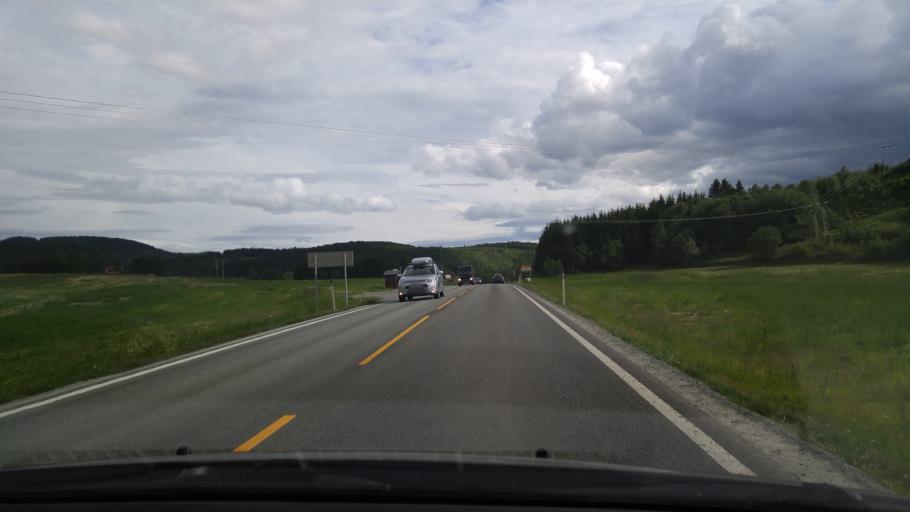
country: NO
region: Nord-Trondelag
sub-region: Verdal
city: Verdal
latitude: 63.8848
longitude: 11.4268
